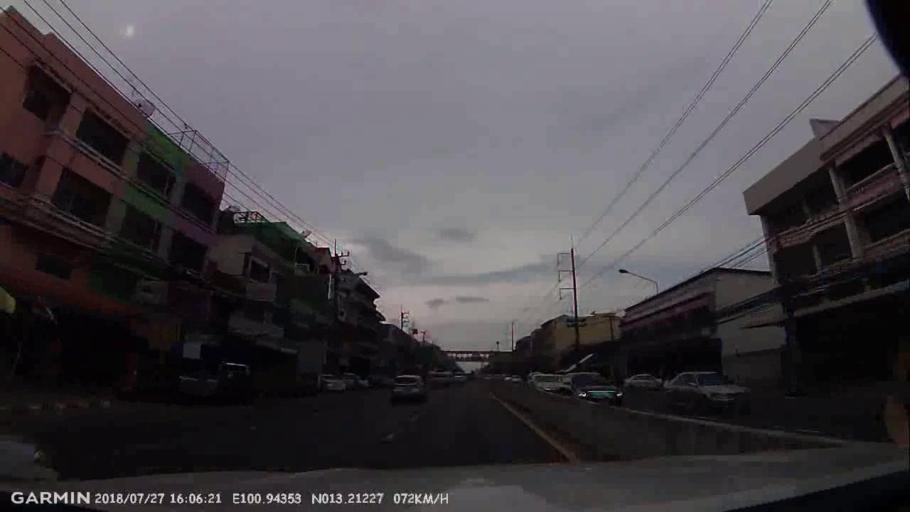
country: TH
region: Chon Buri
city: Si Racha
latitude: 13.2123
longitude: 100.9435
